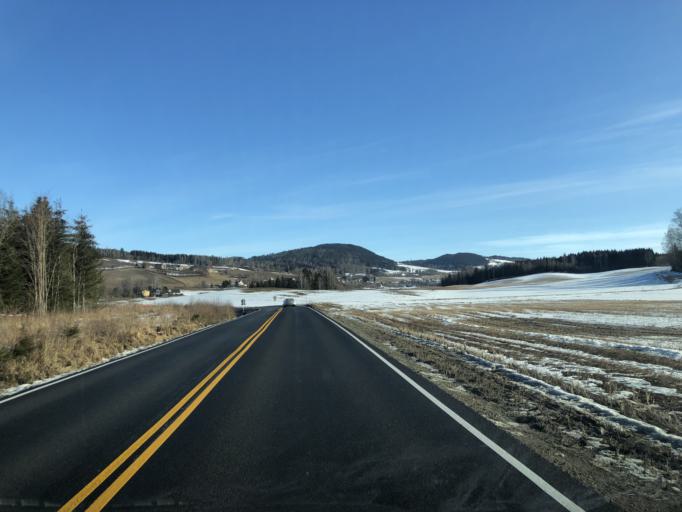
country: NO
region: Hedmark
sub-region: Ringsaker
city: Moelv
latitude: 60.9052
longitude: 10.7346
